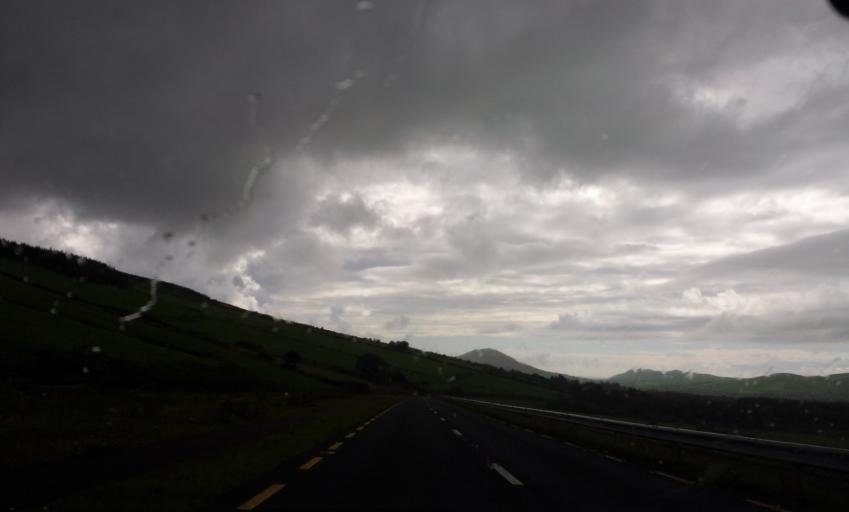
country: IE
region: Munster
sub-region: Ciarrai
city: Killorglin
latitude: 52.1675
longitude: -10.0081
